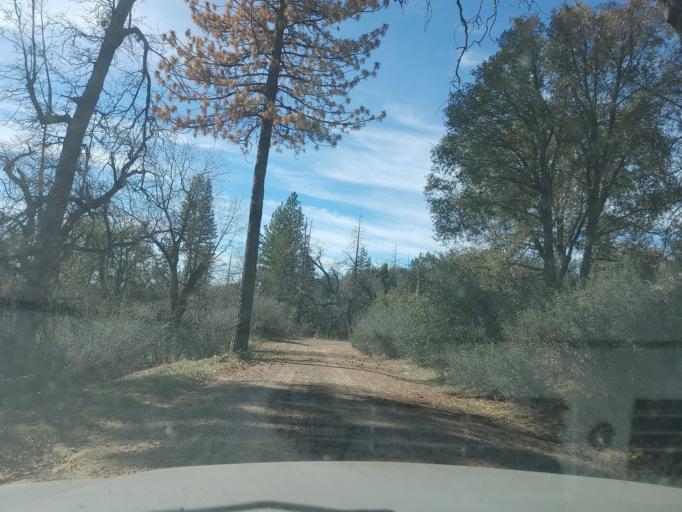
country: US
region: California
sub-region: Madera County
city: Ahwahnee
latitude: 37.4202
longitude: -119.6873
